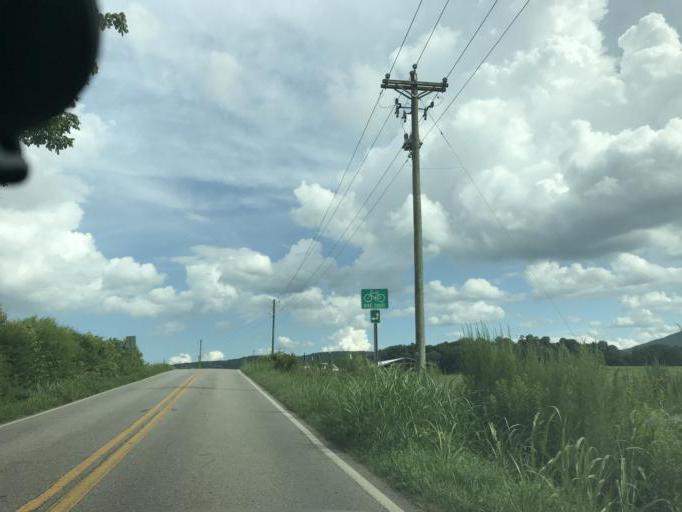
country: US
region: Georgia
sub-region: Forsyth County
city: Cumming
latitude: 34.2727
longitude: -84.1517
